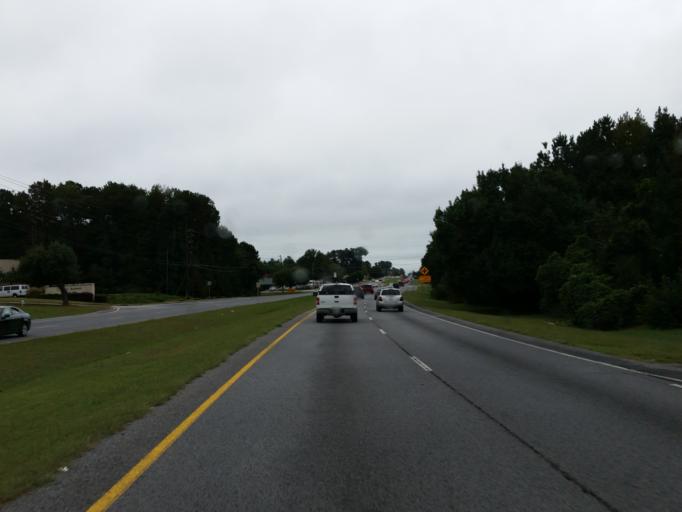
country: US
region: Georgia
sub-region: Clayton County
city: Irondale
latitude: 33.4943
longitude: -84.3429
